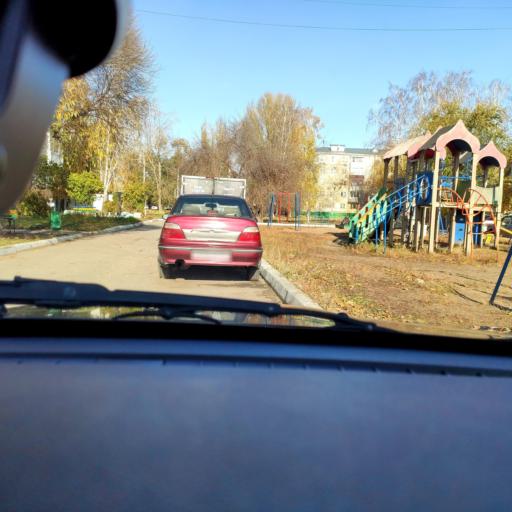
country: RU
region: Samara
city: Tol'yatti
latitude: 53.5315
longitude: 49.4263
